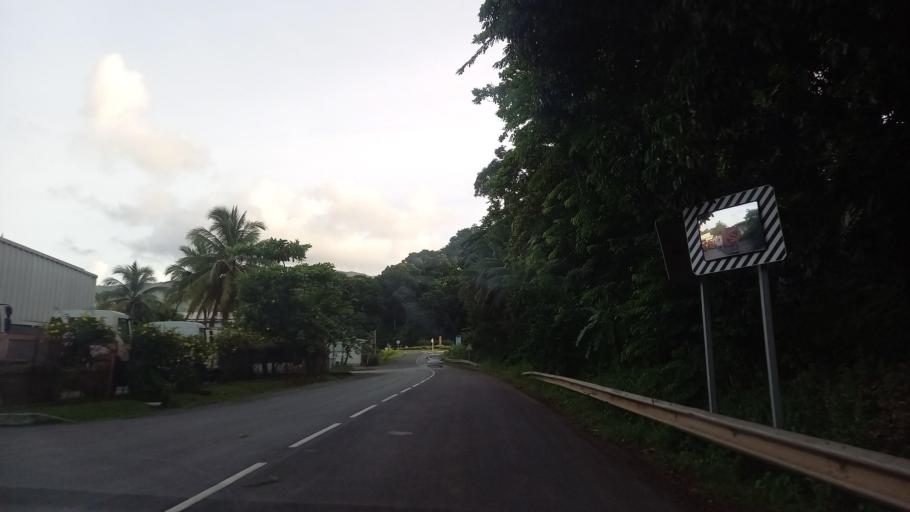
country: YT
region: Koungou
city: Koungou
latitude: -12.7278
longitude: 45.1697
